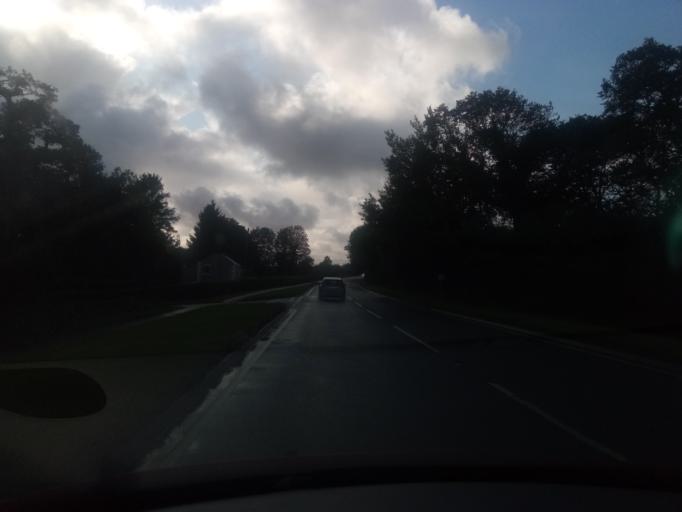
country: GB
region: England
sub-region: Cumbria
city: Carlisle
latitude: 54.9458
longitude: -2.9435
